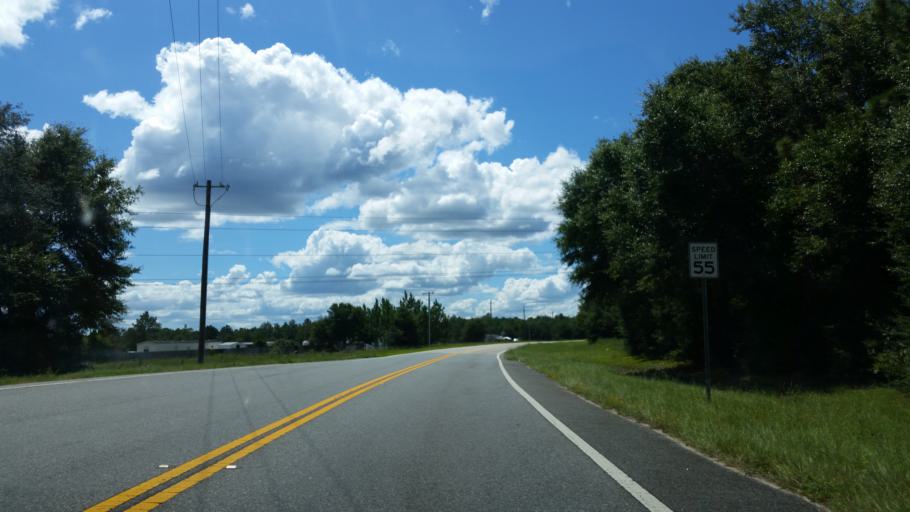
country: US
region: Florida
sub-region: Santa Rosa County
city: East Milton
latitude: 30.5949
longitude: -86.9427
